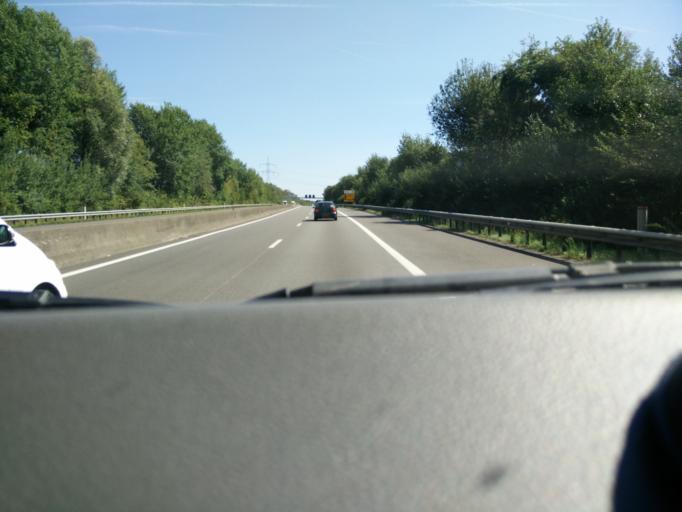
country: LU
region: Luxembourg
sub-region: Canton de Luxembourg
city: Bertrange
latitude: 49.6303
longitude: 6.0523
